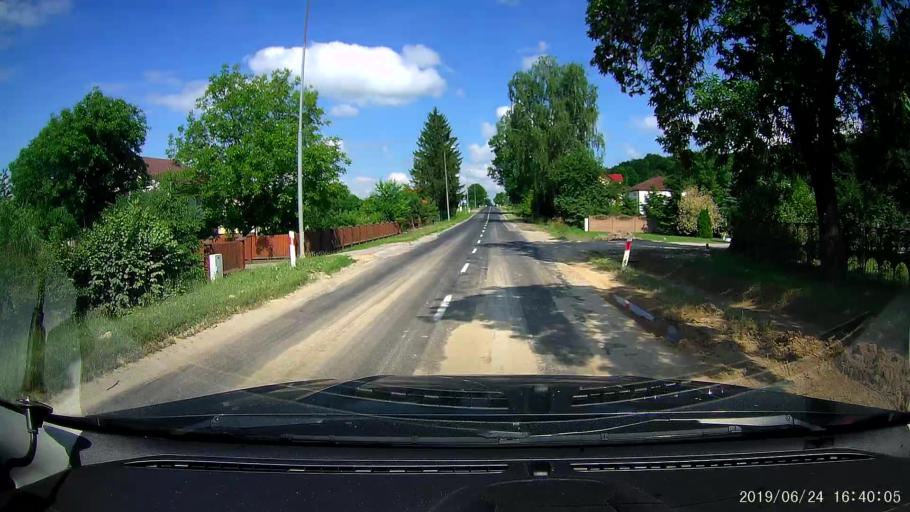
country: PL
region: Lublin Voivodeship
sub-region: Powiat tomaszowski
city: Rachanie
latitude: 50.5299
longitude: 23.5645
